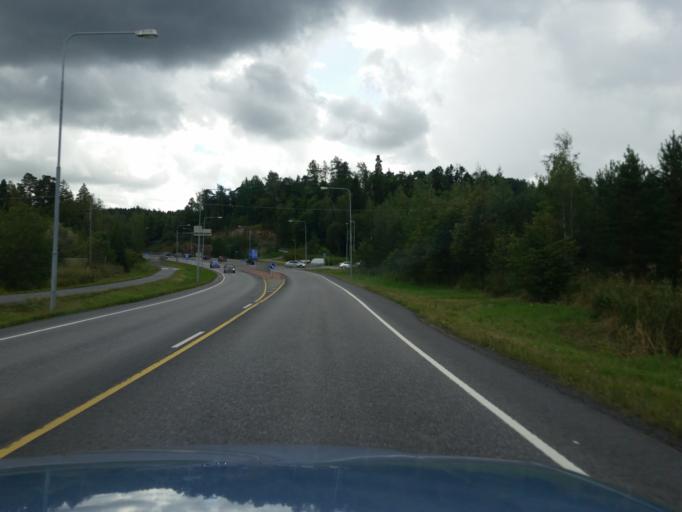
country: FI
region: Varsinais-Suomi
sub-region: Turku
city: Kaarina
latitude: 60.4002
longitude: 22.3875
